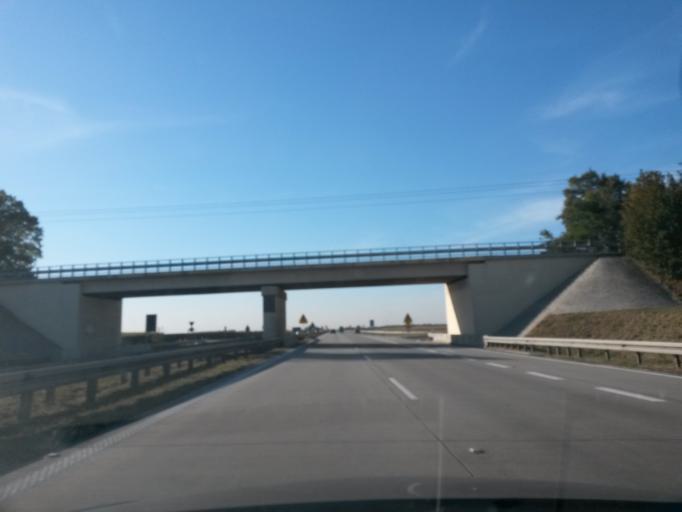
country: PL
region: Lower Silesian Voivodeship
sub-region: Powiat sredzki
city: Udanin
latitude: 51.0704
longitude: 16.4672
